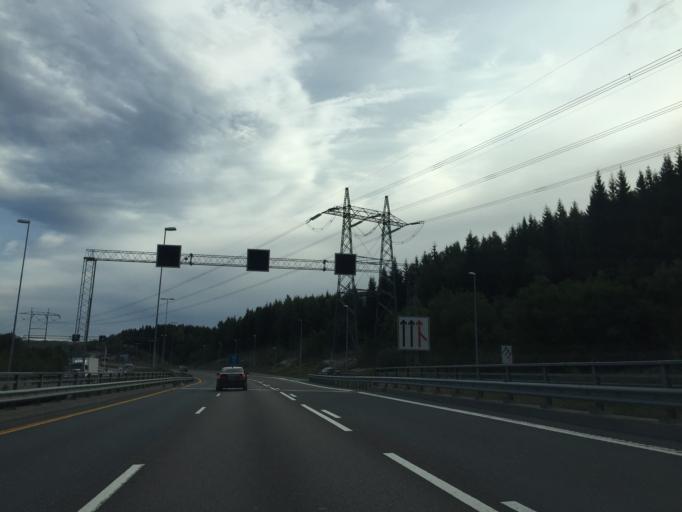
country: NO
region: Akershus
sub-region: Oppegard
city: Kolbotn
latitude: 59.7725
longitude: 10.8337
